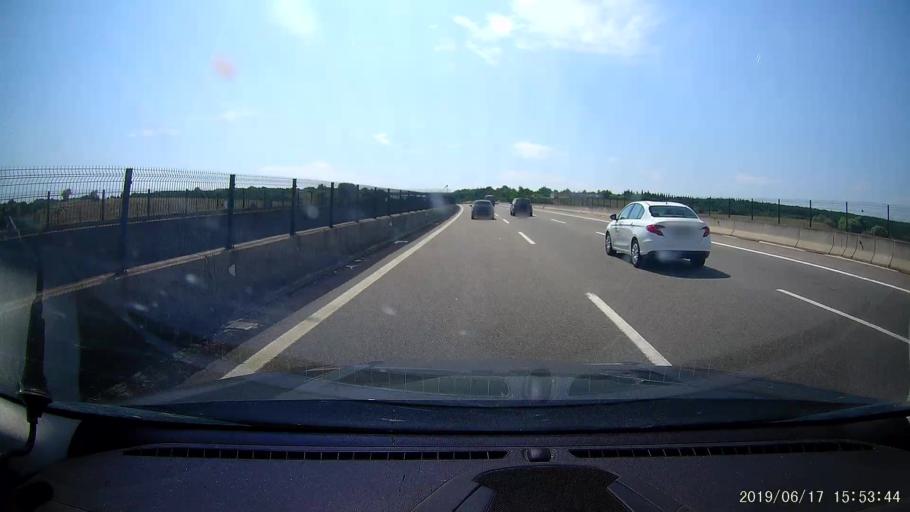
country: TR
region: Istanbul
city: Buyukcavuslu
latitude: 41.2020
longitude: 28.0654
